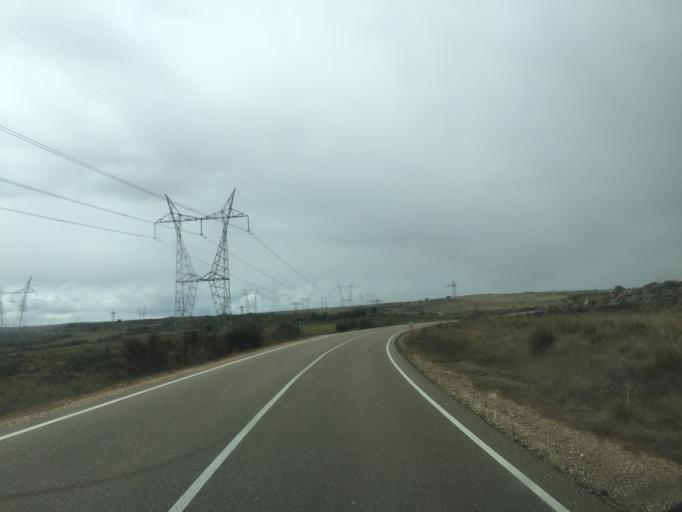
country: ES
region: Castille and Leon
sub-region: Provincia de Zamora
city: Villalcampo
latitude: 41.5291
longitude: -5.9967
